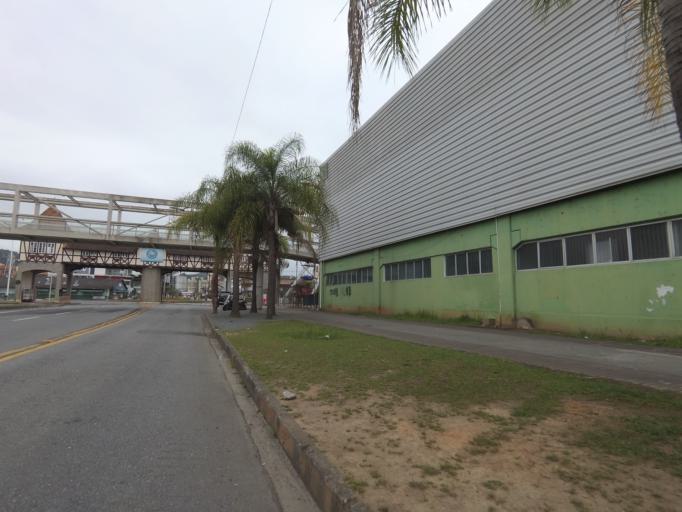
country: BR
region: Santa Catarina
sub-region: Blumenau
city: Blumenau
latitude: -26.9156
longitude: -49.0863
